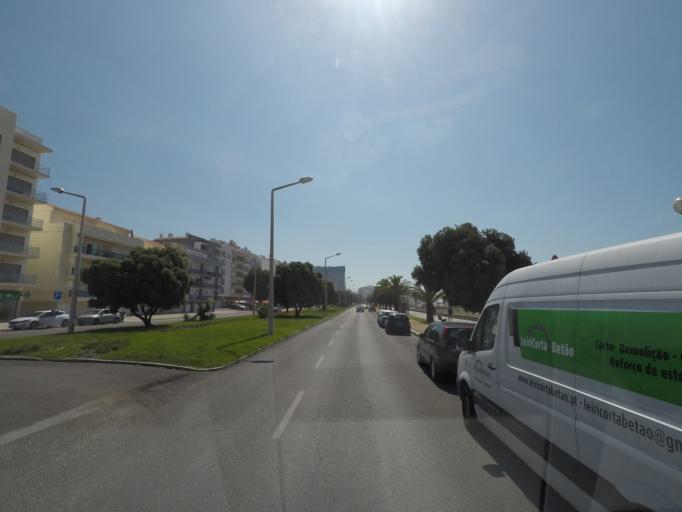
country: PT
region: Coimbra
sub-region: Figueira da Foz
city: Buarcos
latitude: 40.1597
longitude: -8.8703
